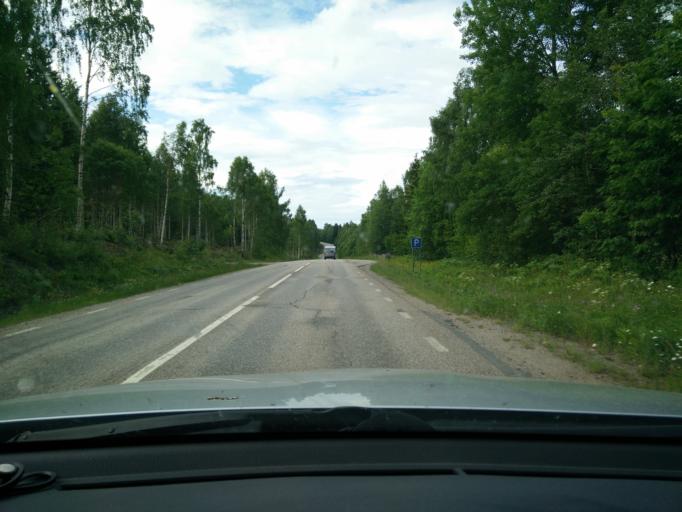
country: SE
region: Gaevleborg
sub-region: Nordanstigs Kommun
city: Bergsjoe
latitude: 61.9621
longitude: 17.0618
